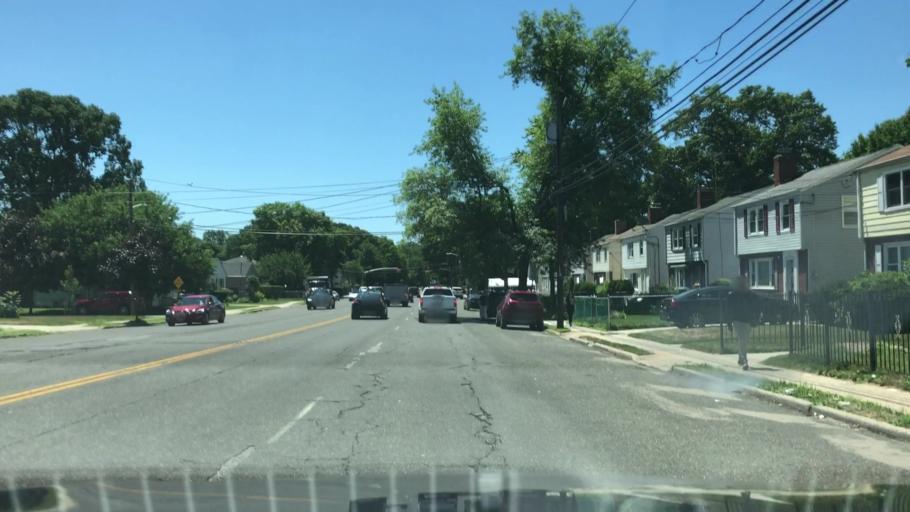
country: US
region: New York
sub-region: Nassau County
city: Hempstead
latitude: 40.7004
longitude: -73.6313
